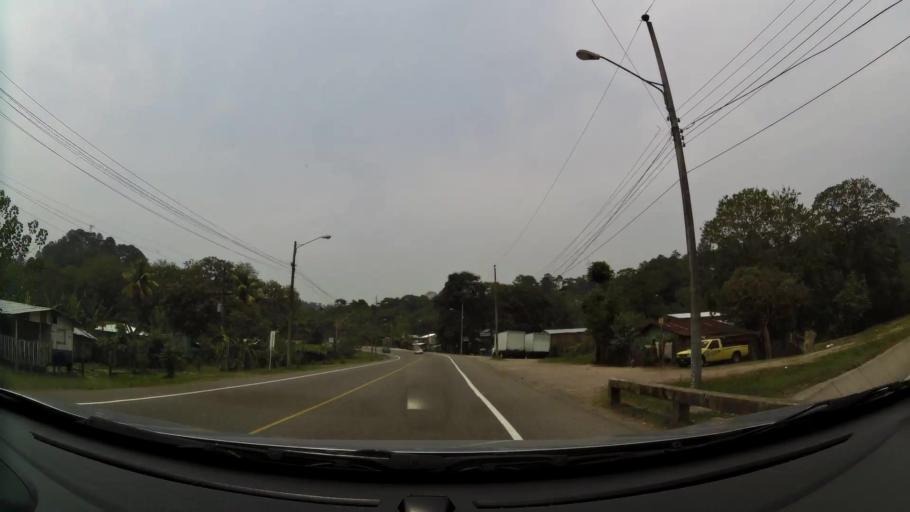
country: HN
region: Cortes
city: La Guama
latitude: 14.8841
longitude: -87.9376
